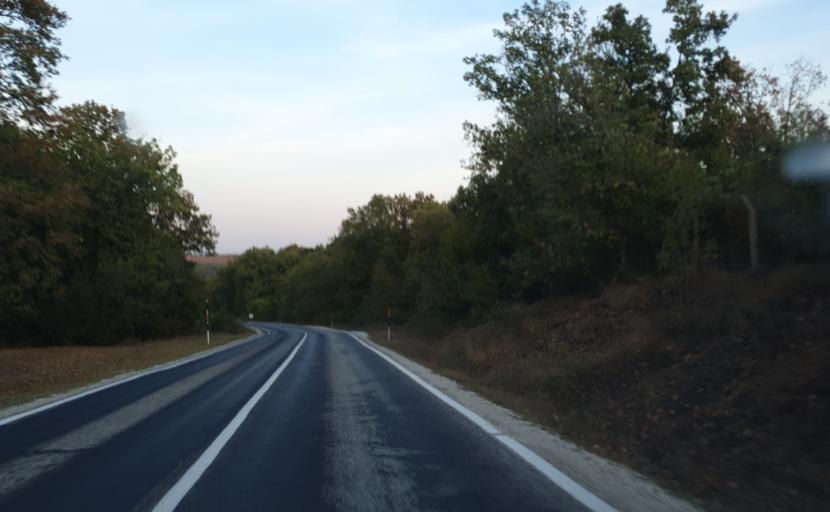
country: TR
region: Kirklareli
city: Igneada
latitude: 41.8796
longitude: 27.8925
